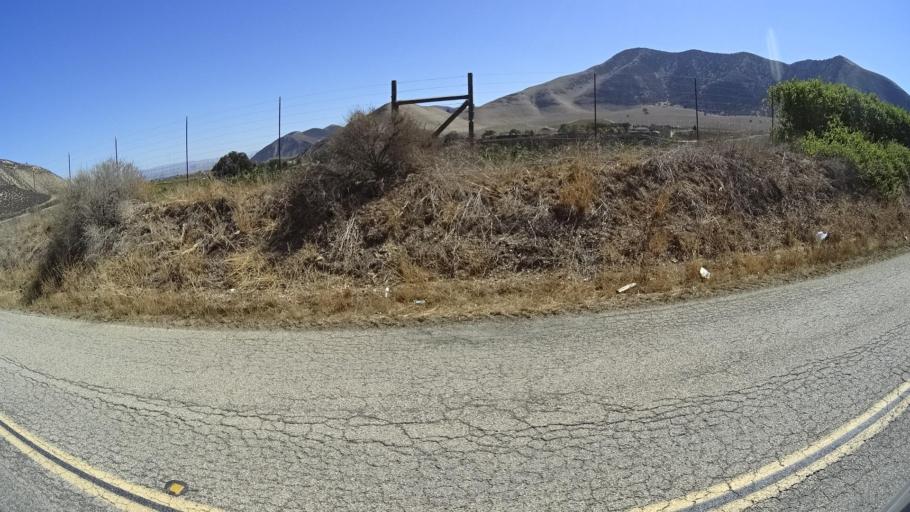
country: US
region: California
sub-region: Monterey County
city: Greenfield
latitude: 36.2768
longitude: -121.3336
